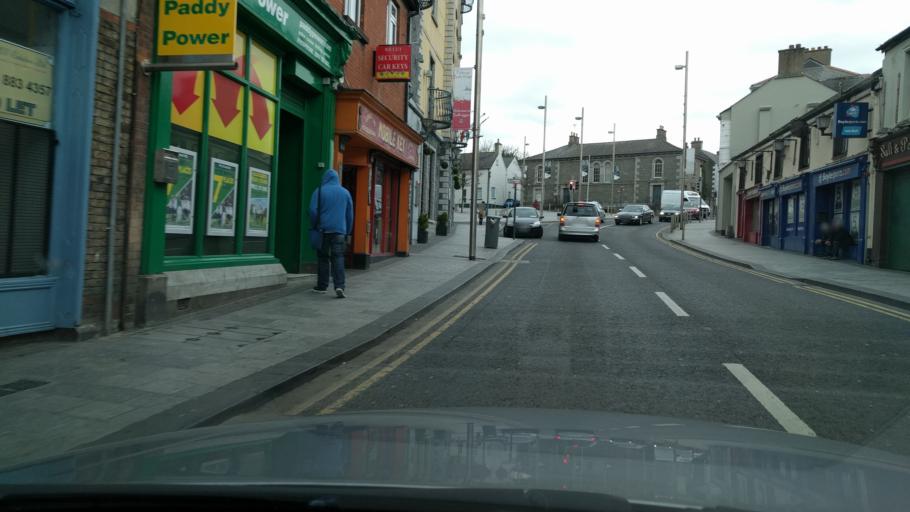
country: IE
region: Leinster
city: Balbriggan
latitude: 53.6092
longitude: -6.1833
